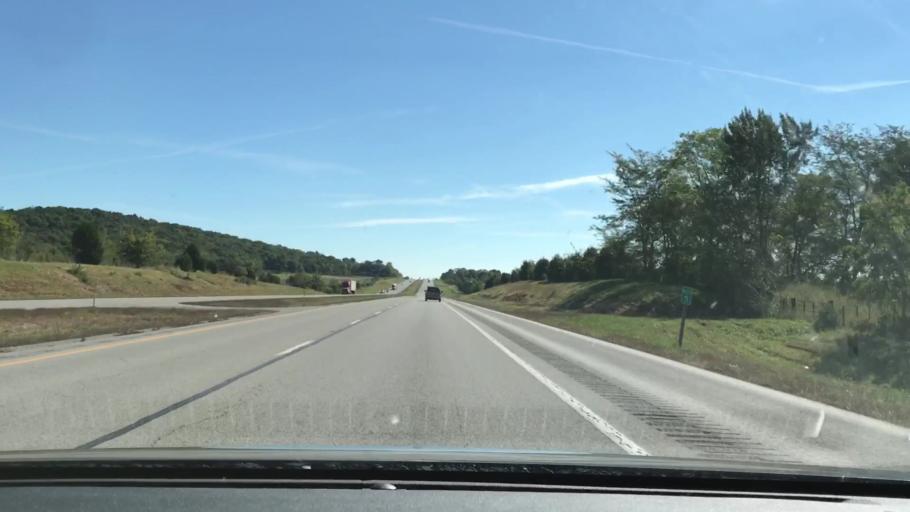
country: US
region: Kentucky
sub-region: Todd County
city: Elkton
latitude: 36.8259
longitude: -87.2165
